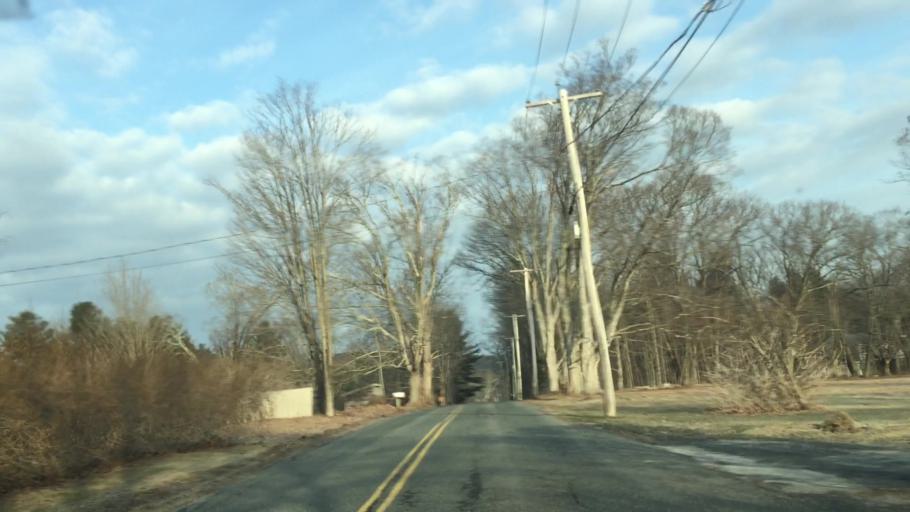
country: US
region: Massachusetts
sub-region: Berkshire County
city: New Marlborough
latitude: 42.1576
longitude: -73.2696
